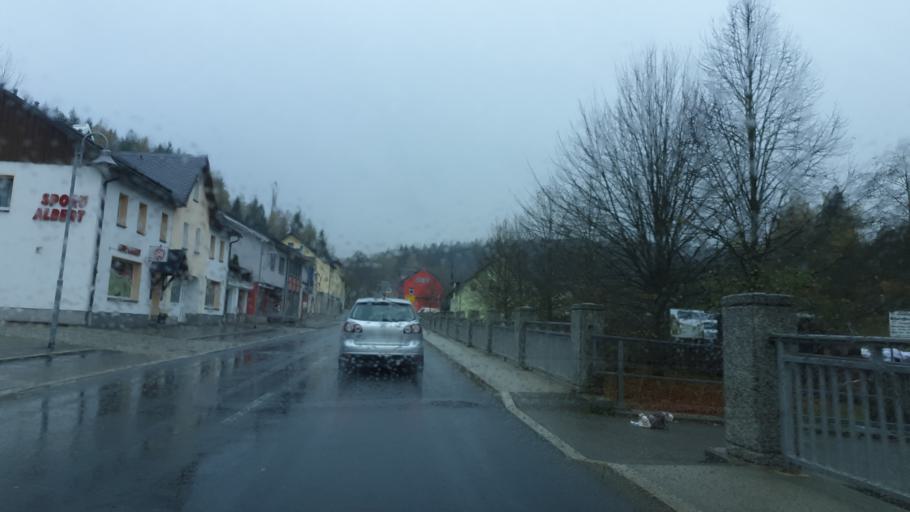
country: DE
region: Saxony
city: Tannenbergsthal
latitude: 50.4374
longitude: 12.4616
